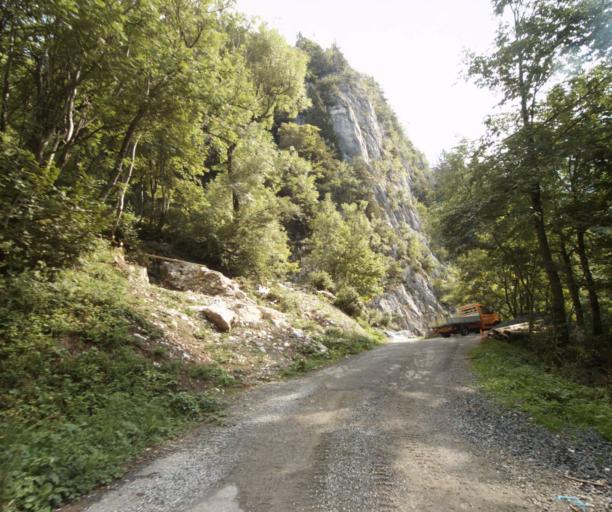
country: CH
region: Vaud
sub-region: Riviera-Pays-d'Enhaut District
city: Caux
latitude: 46.4215
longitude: 6.9790
